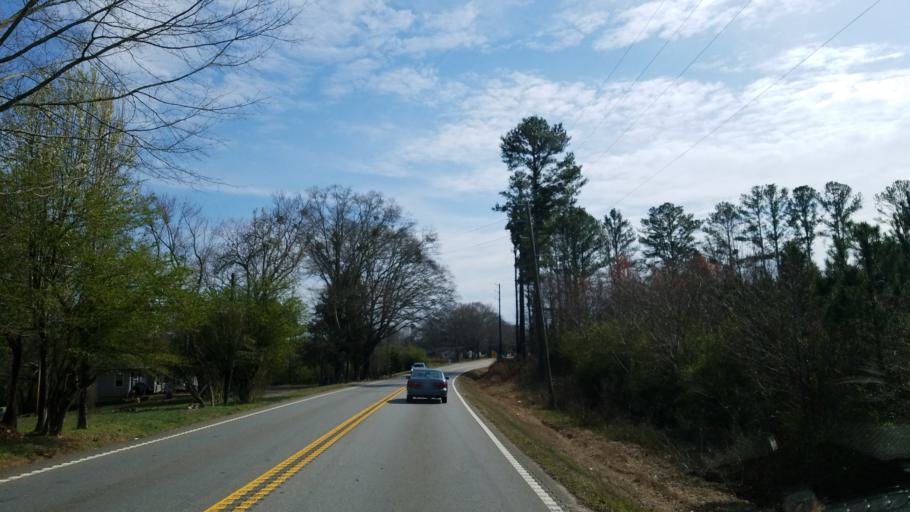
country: US
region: Georgia
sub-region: Cherokee County
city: Canton
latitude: 34.2120
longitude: -84.4561
